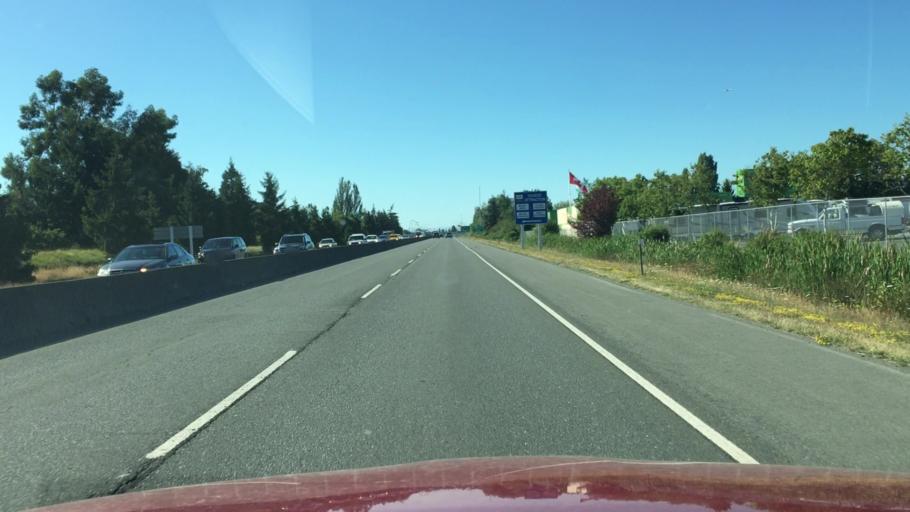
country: CA
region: British Columbia
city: North Saanich
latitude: 48.6550
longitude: -123.4115
